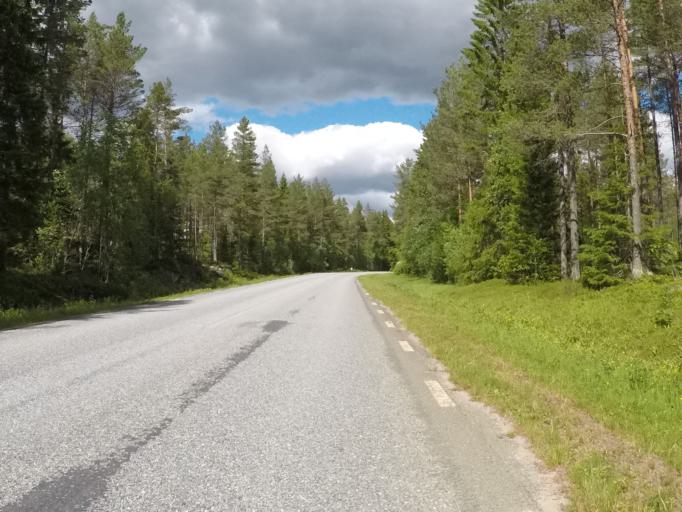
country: SE
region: Vaesterbotten
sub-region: Robertsfors Kommun
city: Robertsfors
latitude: 63.9726
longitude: 20.8107
